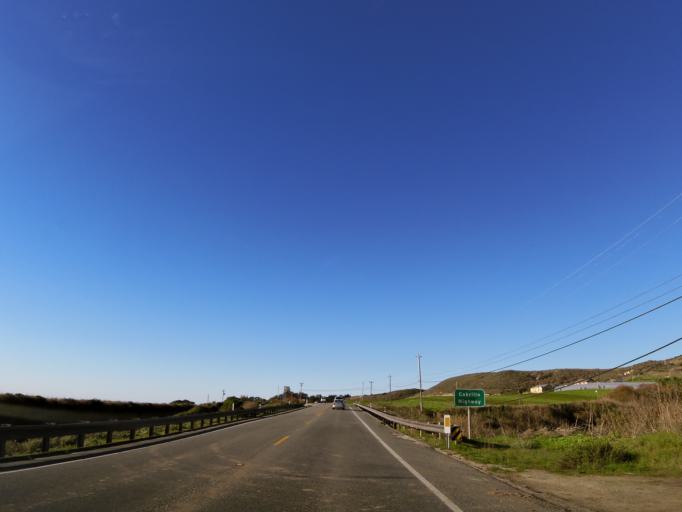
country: US
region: California
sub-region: Santa Cruz County
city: Bonny Doon
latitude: 37.0048
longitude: -122.1845
